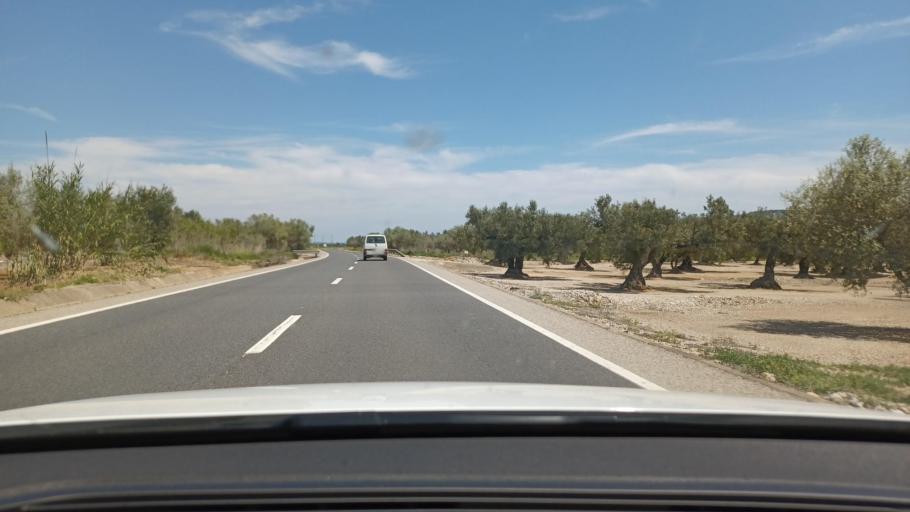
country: ES
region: Catalonia
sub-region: Provincia de Tarragona
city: Ulldecona
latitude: 40.6637
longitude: 0.4250
